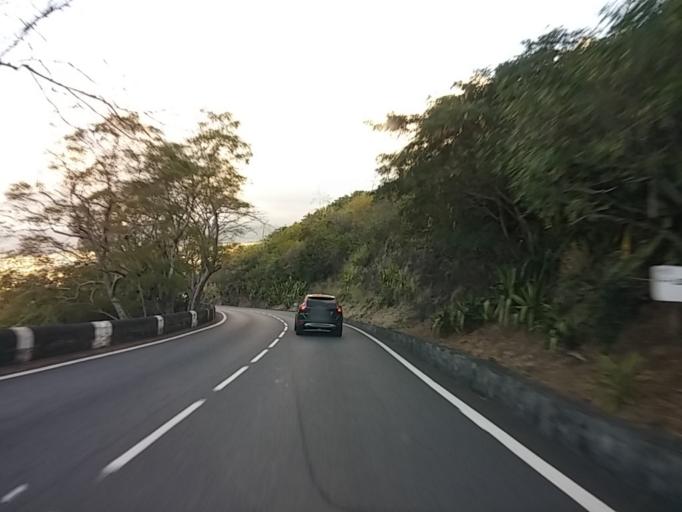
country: RE
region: Reunion
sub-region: Reunion
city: Saint-Denis
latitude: -20.8864
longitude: 55.4337
